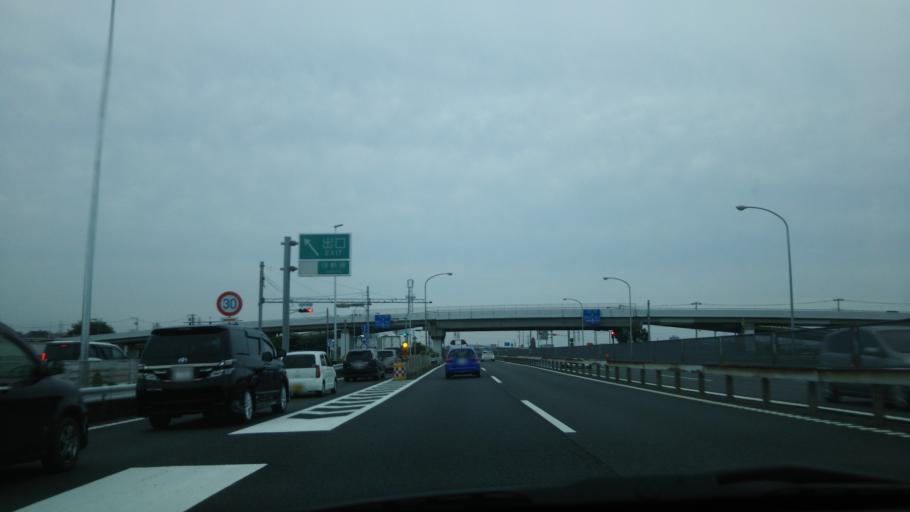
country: JP
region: Kanagawa
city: Isehara
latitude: 35.3849
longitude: 139.3308
